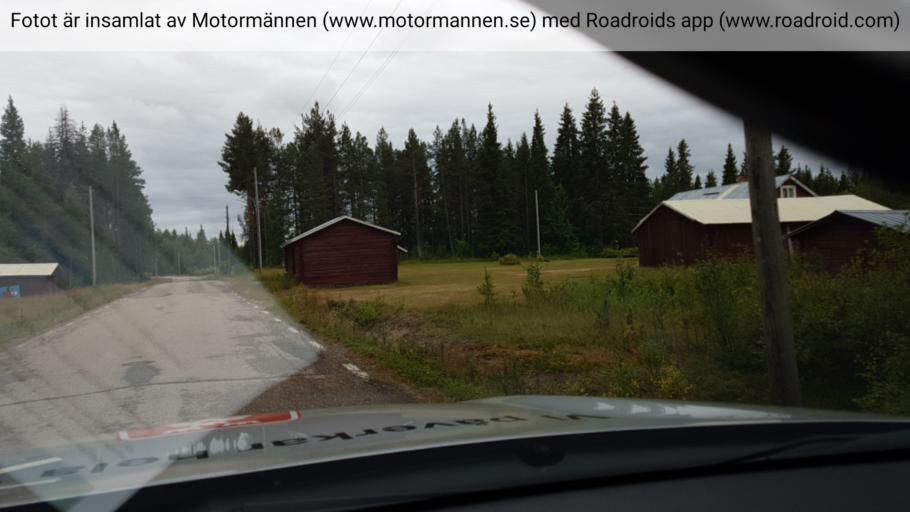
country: SE
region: Norrbotten
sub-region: Pajala Kommun
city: Pajala
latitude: 67.1350
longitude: 22.6495
